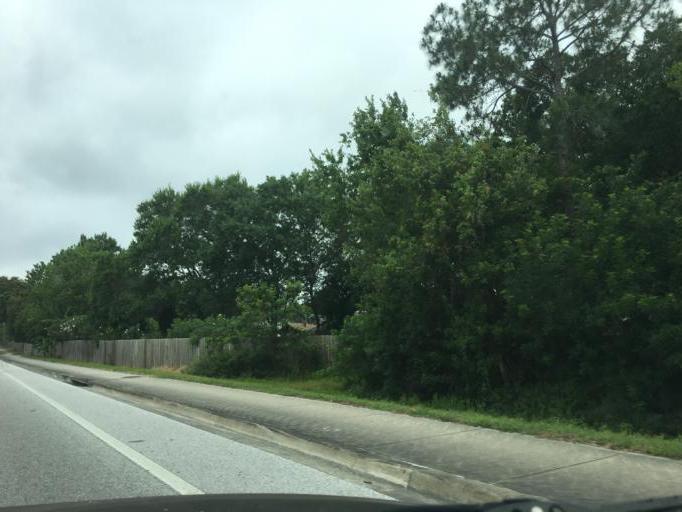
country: US
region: Florida
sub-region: Pinellas County
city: Dunedin
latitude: 28.0114
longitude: -82.7633
